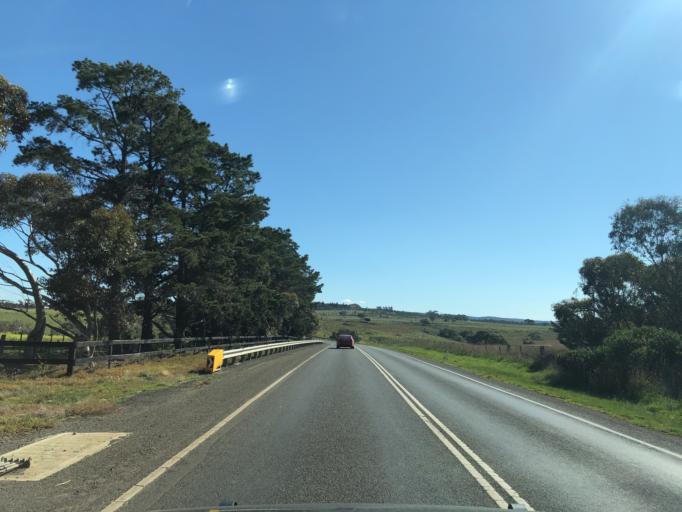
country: AU
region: Victoria
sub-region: Hume
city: Diggers Rest
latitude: -37.6254
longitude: 144.6632
